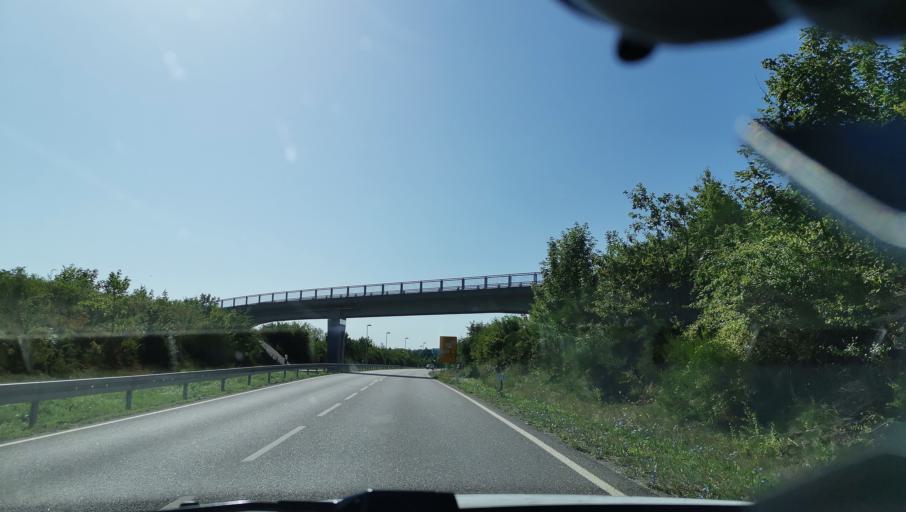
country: DE
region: Bavaria
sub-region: Regierungsbezirk Mittelfranken
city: Zirndorf
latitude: 49.4417
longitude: 10.9351
